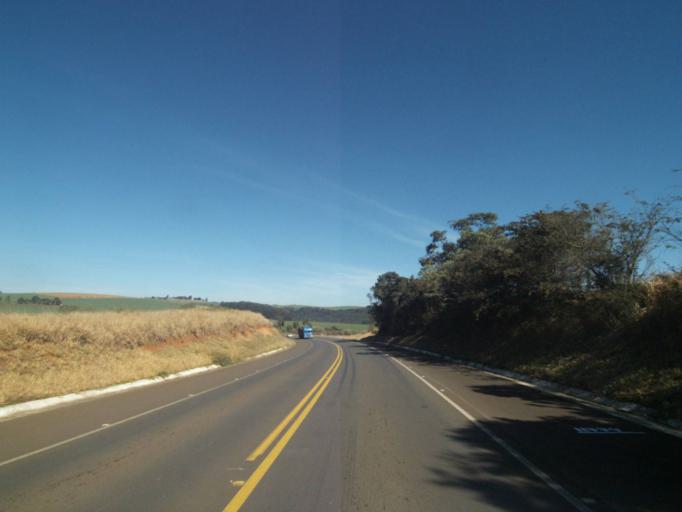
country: BR
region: Parana
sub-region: Tibagi
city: Tibagi
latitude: -24.7391
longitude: -50.4583
